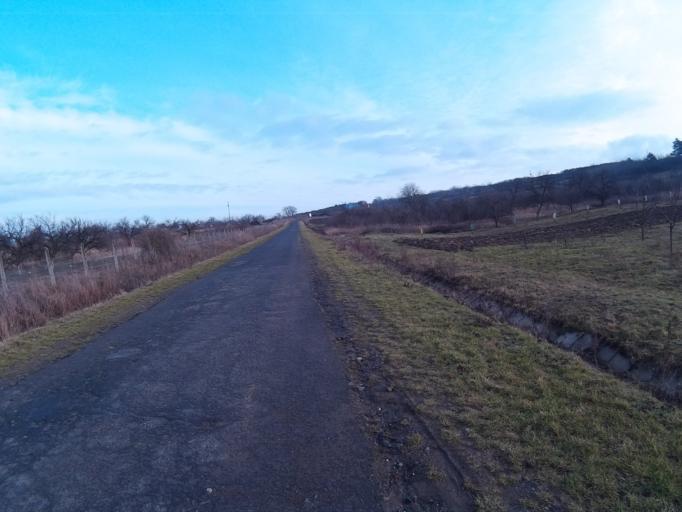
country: HU
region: Borsod-Abauj-Zemplen
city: Abaujszanto
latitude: 48.3448
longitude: 21.2284
